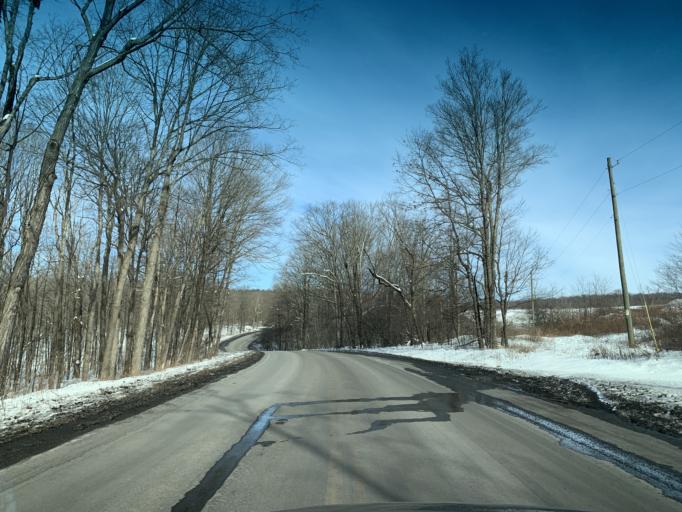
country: US
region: Maryland
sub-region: Allegany County
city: Frostburg
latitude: 39.6184
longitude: -78.9255
